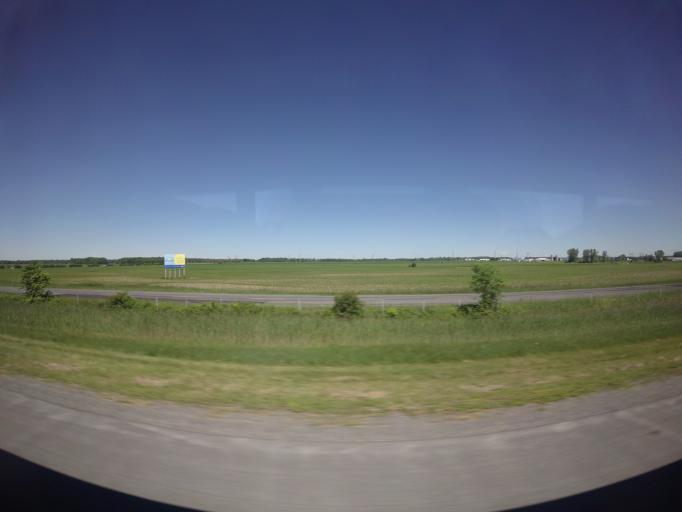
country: CA
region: Quebec
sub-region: Mauricie
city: Saint-Germain-de-Grantham
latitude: 45.7468
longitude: -72.7201
